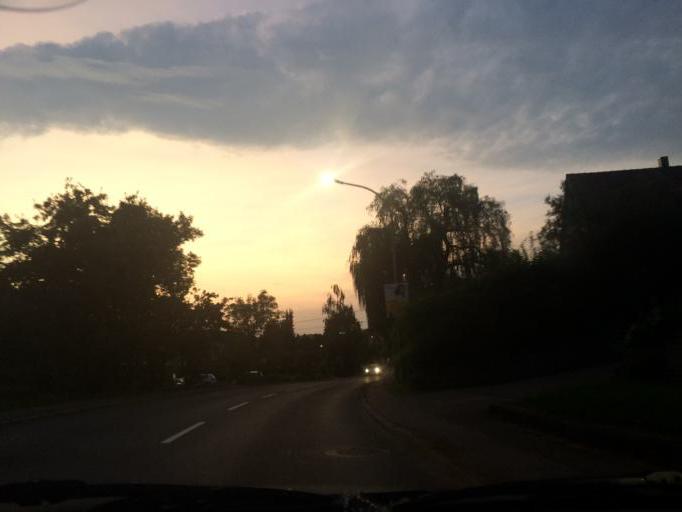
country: DE
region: Baden-Wuerttemberg
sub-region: Regierungsbezirk Stuttgart
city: Schorndorf
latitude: 48.8273
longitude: 9.5170
